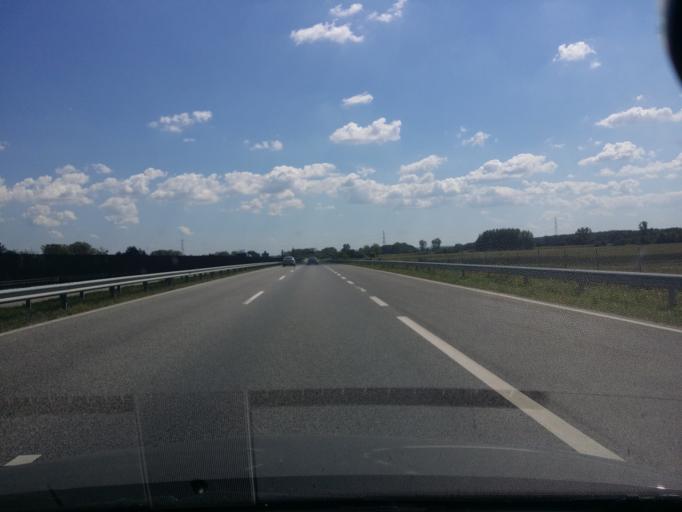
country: HU
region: Gyor-Moson-Sopron
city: Rabapatona
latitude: 47.6532
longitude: 17.4304
